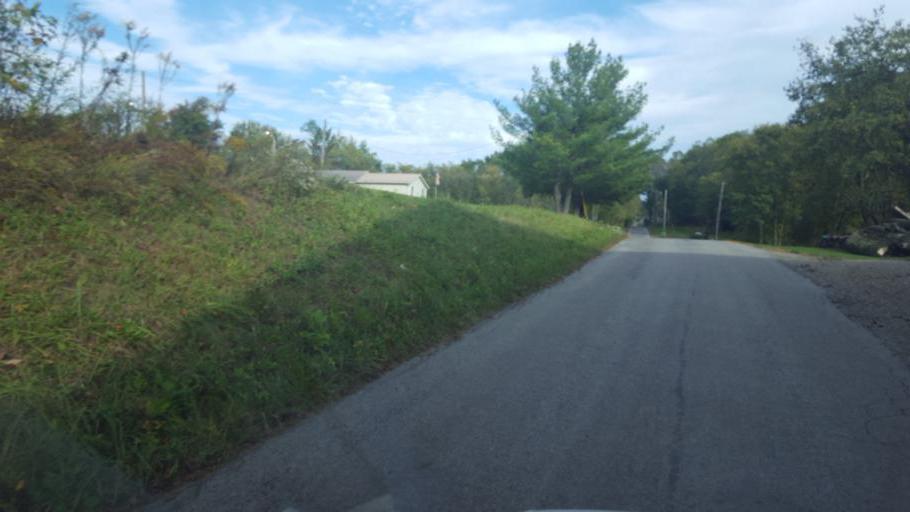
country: US
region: Ohio
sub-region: Holmes County
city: Millersburg
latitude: 40.5408
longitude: -81.8693
